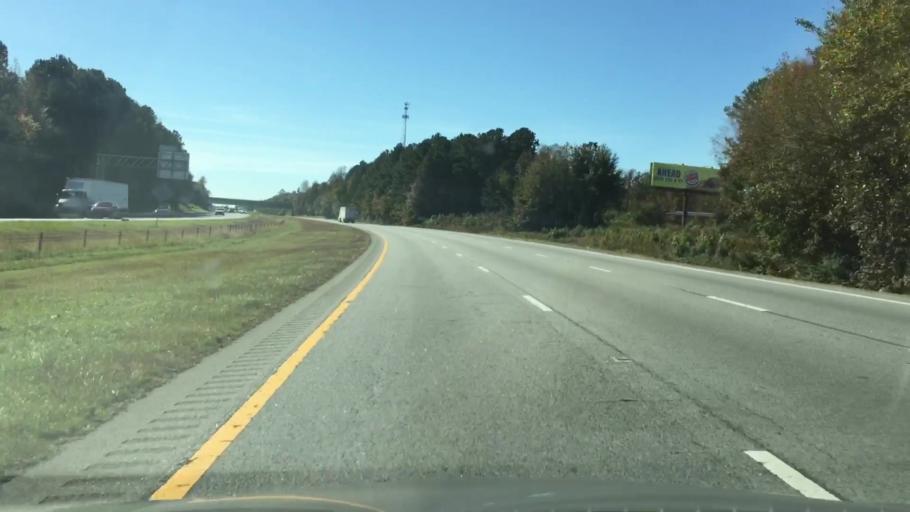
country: US
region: North Carolina
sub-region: Randolph County
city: Archdale
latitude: 35.8966
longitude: -79.9706
